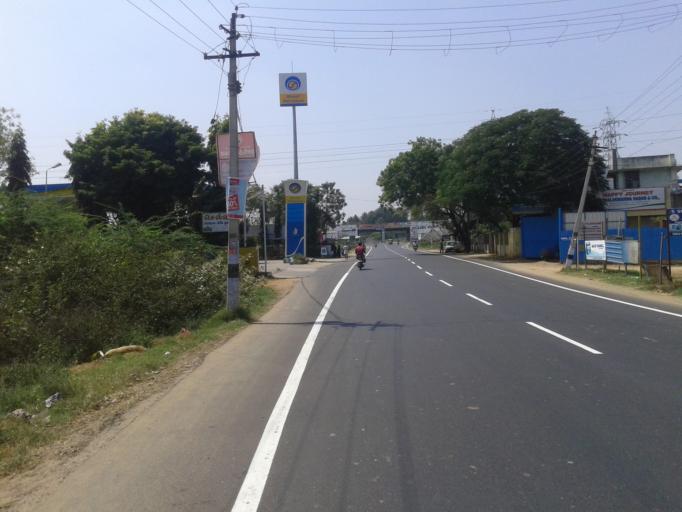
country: IN
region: Tamil Nadu
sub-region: Madurai
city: Tirupparangunram
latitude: 9.9384
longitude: 78.0611
